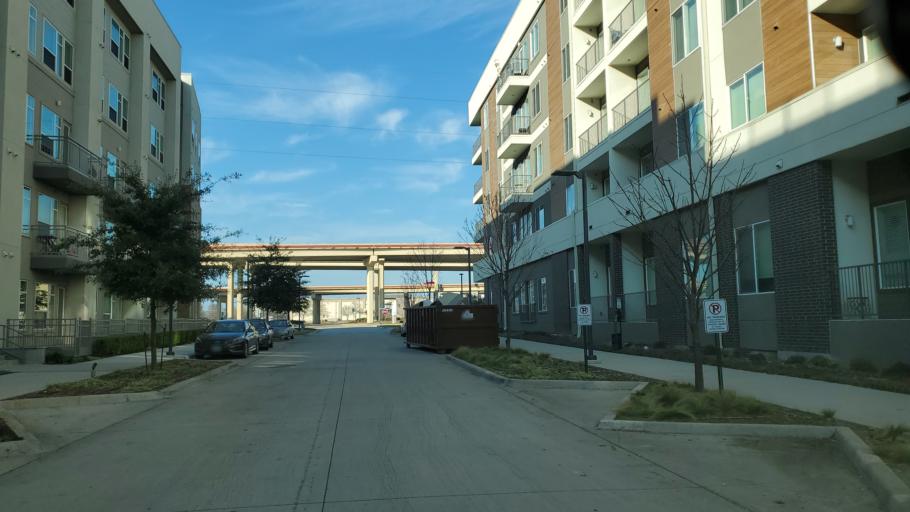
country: US
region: Texas
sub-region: Collin County
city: Plano
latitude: 33.0021
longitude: -96.7049
